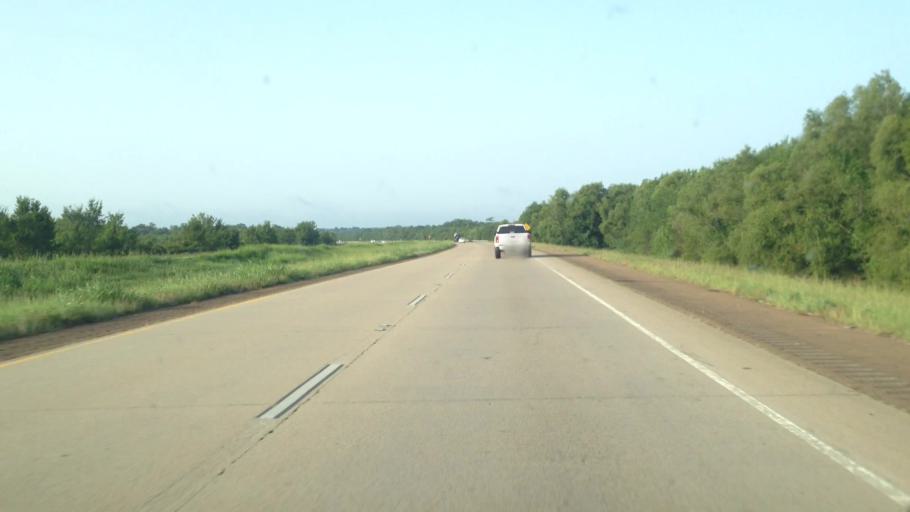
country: US
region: Louisiana
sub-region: Rapides Parish
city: Woodworth
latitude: 31.2074
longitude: -92.4726
